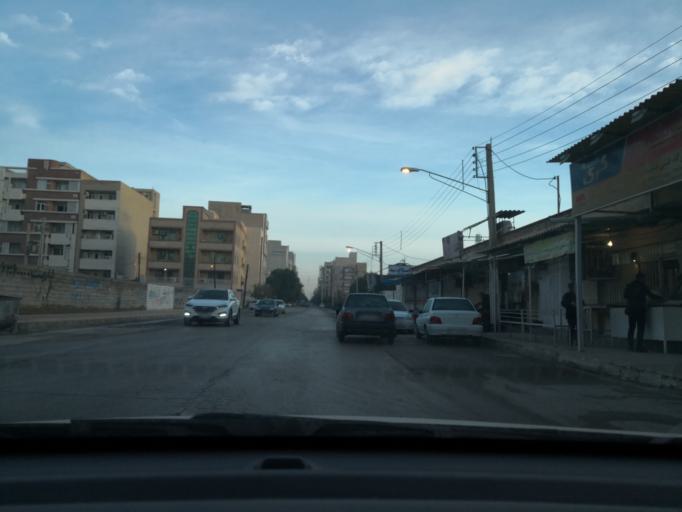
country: IR
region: Khuzestan
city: Ahvaz
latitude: 31.3513
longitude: 48.6785
